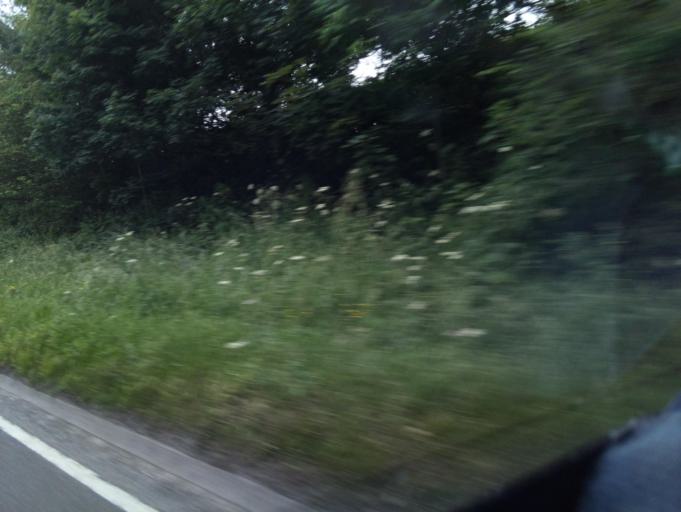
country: GB
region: England
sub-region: Staffordshire
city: Mayfield
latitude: 52.9327
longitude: -1.7634
